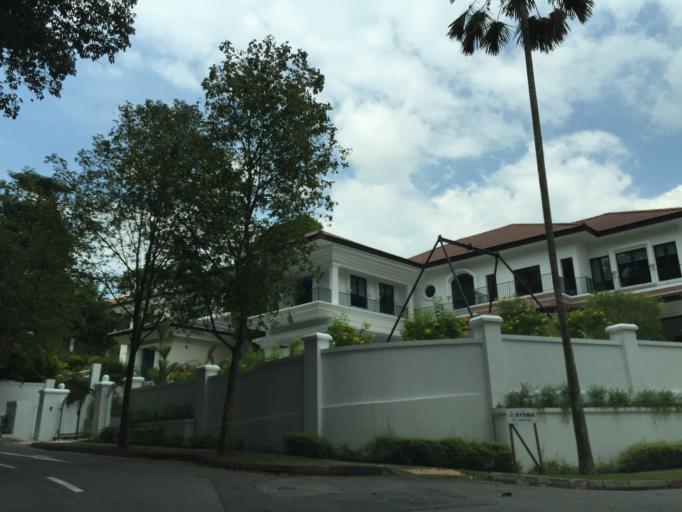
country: SG
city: Singapore
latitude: 1.3044
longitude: 103.8072
